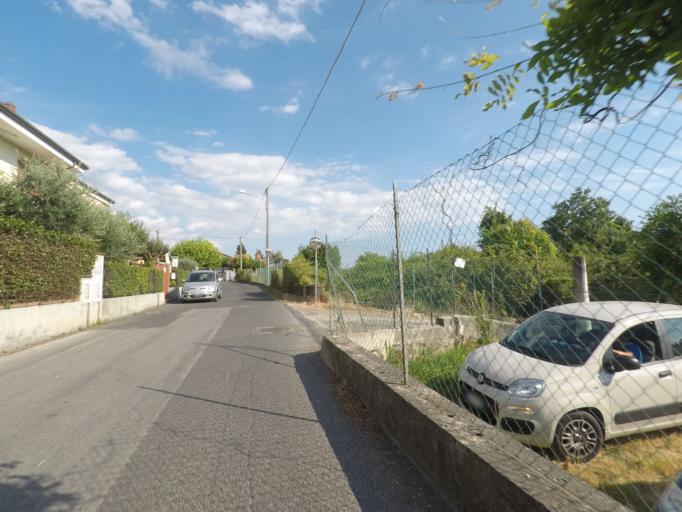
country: IT
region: Tuscany
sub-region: Provincia di Massa-Carrara
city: Massa
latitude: 44.0200
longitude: 10.1433
